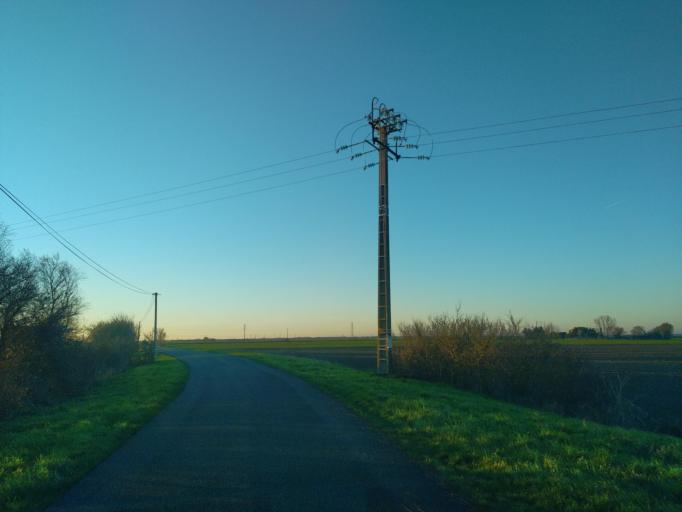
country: FR
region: Pays de la Loire
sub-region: Departement de la Vendee
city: Angles
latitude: 46.3804
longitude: -1.3161
